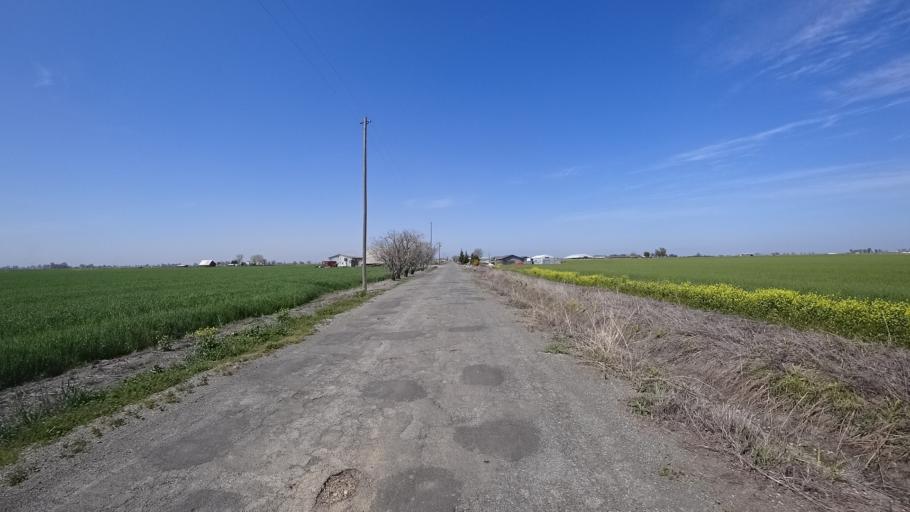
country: US
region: California
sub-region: Glenn County
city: Willows
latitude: 39.5727
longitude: -122.0769
